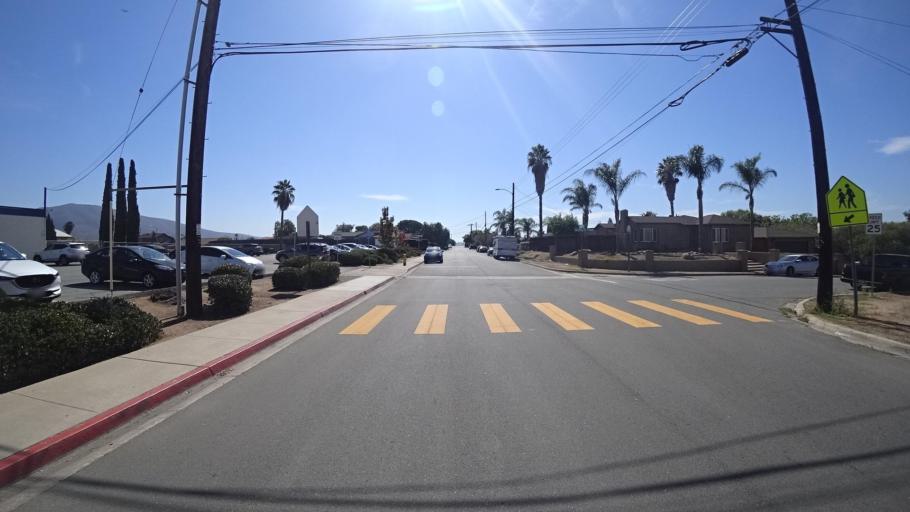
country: US
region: California
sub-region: San Diego County
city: La Presa
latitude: 32.7061
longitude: -116.9933
